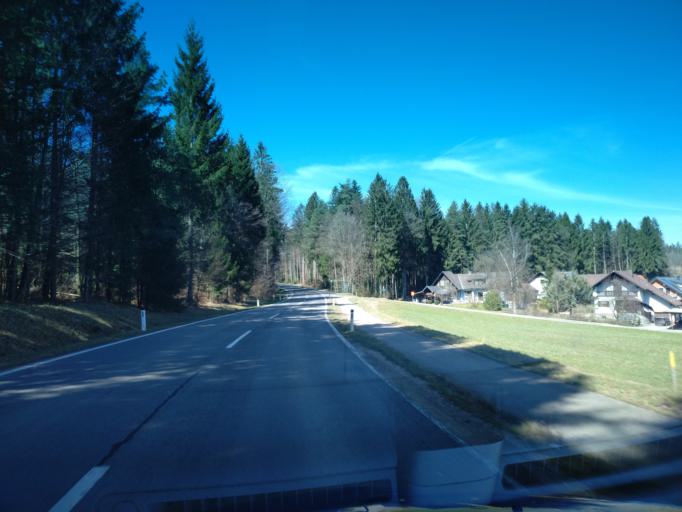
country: AT
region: Styria
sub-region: Politischer Bezirk Deutschlandsberg
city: Sankt Peter im Sulmtal
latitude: 46.7785
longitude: 15.2481
